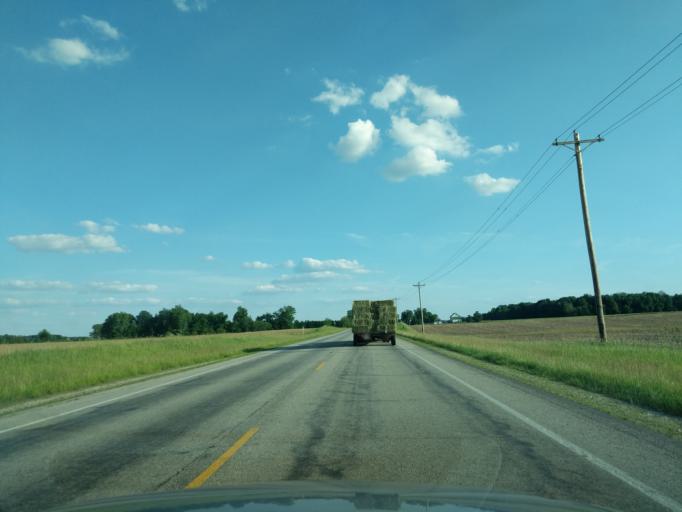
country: US
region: Indiana
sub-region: Huntington County
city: Roanoke
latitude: 41.0334
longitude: -85.4707
